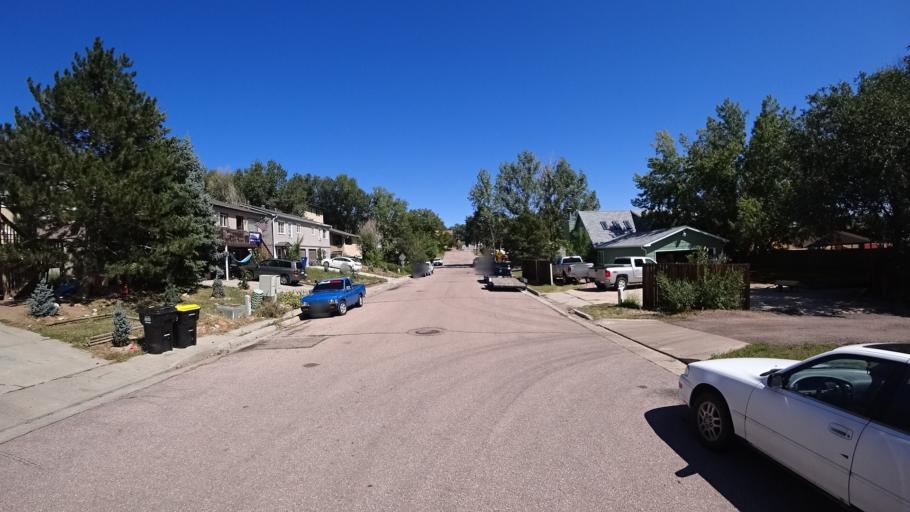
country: US
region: Colorado
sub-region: El Paso County
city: Colorado Springs
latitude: 38.8532
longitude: -104.8591
